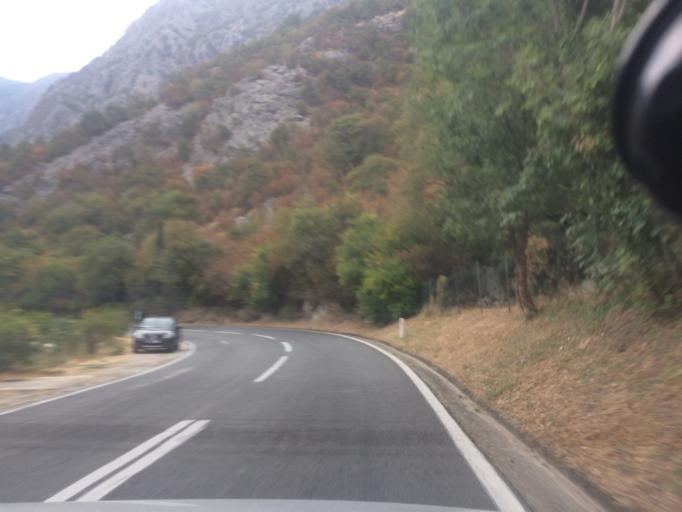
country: ME
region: Kotor
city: Risan
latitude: 42.5026
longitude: 18.6932
